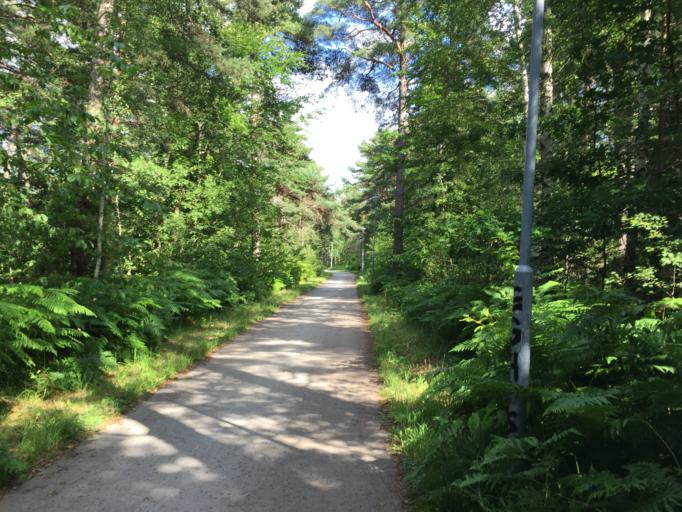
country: SE
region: Gotland
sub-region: Gotland
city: Visby
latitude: 57.6105
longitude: 18.2902
